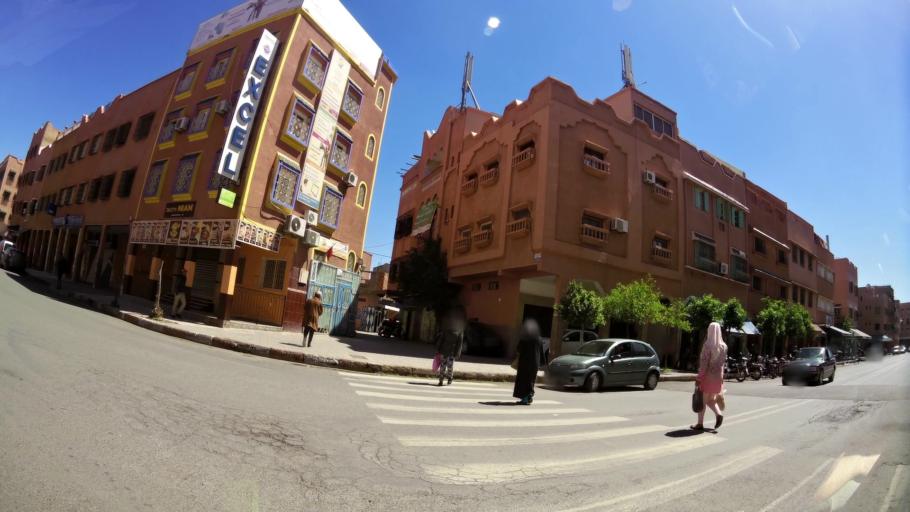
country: MA
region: Marrakech-Tensift-Al Haouz
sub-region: Marrakech
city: Marrakesh
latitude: 31.6329
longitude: -8.0678
